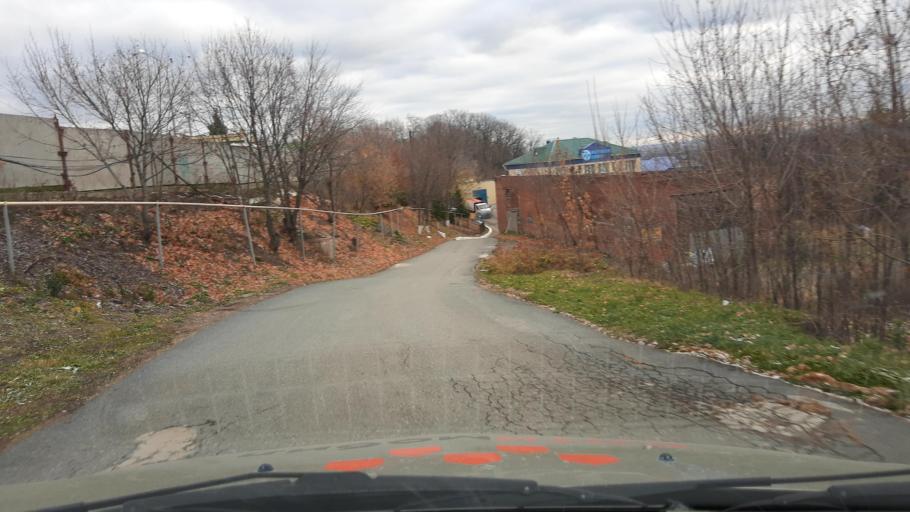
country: RU
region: Bashkortostan
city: Ufa
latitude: 54.7494
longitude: 56.0350
